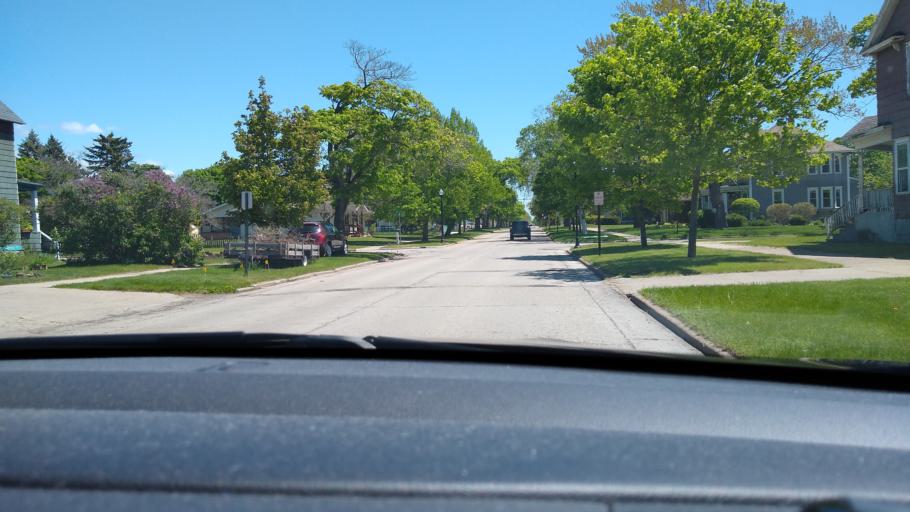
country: US
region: Michigan
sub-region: Delta County
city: Escanaba
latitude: 45.7395
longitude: -87.0662
